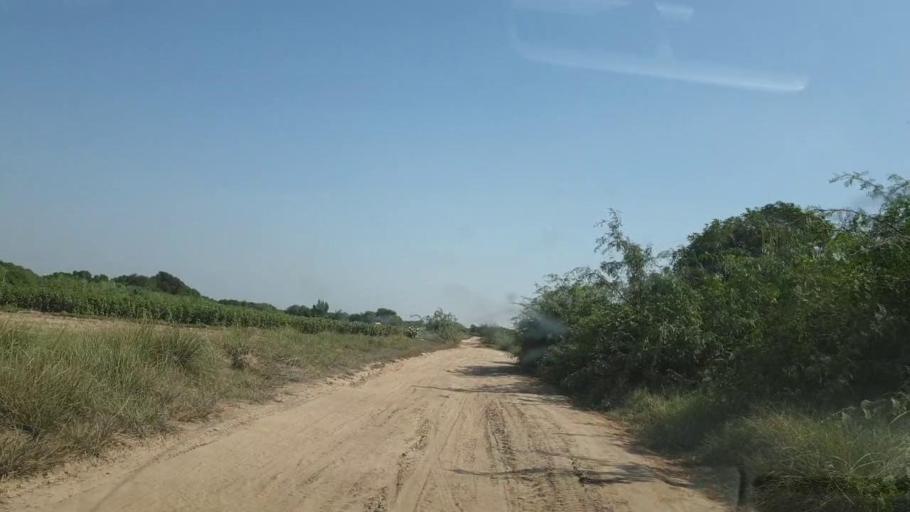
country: PK
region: Sindh
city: Tando Jam
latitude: 25.3695
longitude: 68.5815
